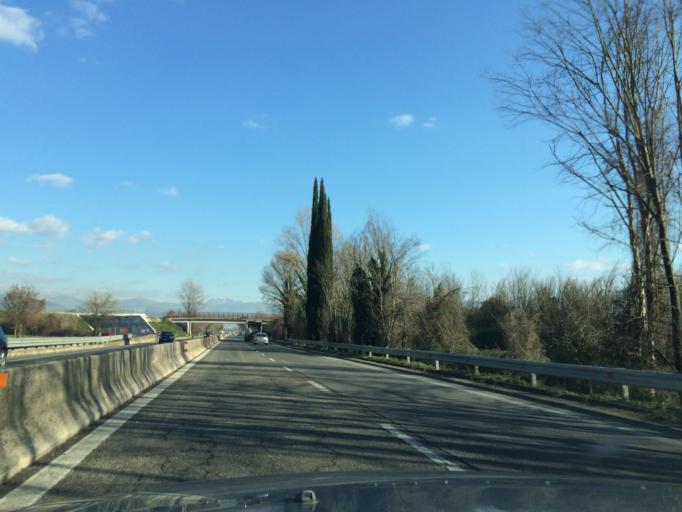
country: IT
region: Umbria
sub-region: Provincia di Terni
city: Terni
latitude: 42.5697
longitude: 12.5948
